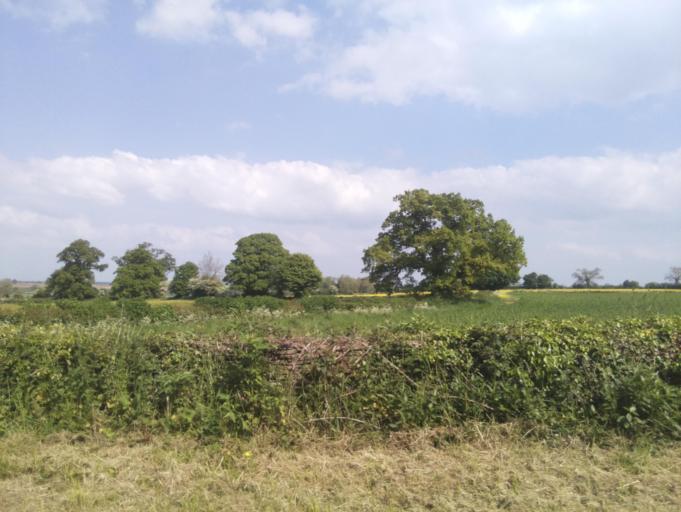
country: GB
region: England
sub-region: Wiltshire
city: Luckington
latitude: 51.5829
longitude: -2.2684
